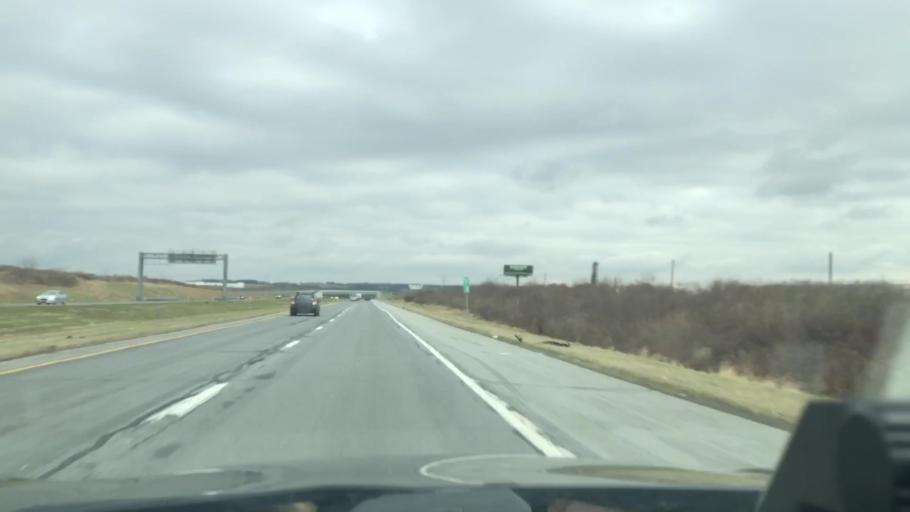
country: US
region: Pennsylvania
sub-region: Northampton County
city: Tatamy
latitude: 40.7312
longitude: -75.2716
